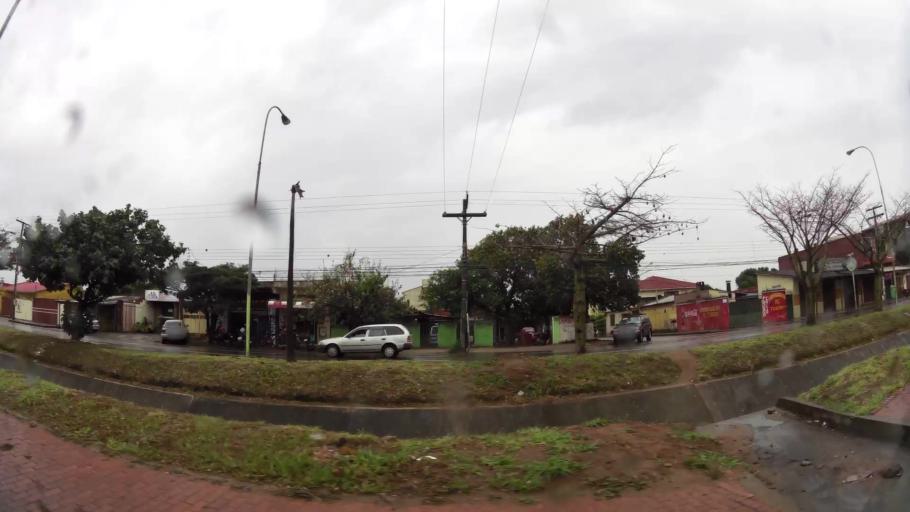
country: BO
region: Santa Cruz
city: Santa Cruz de la Sierra
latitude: -17.7966
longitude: -63.1550
